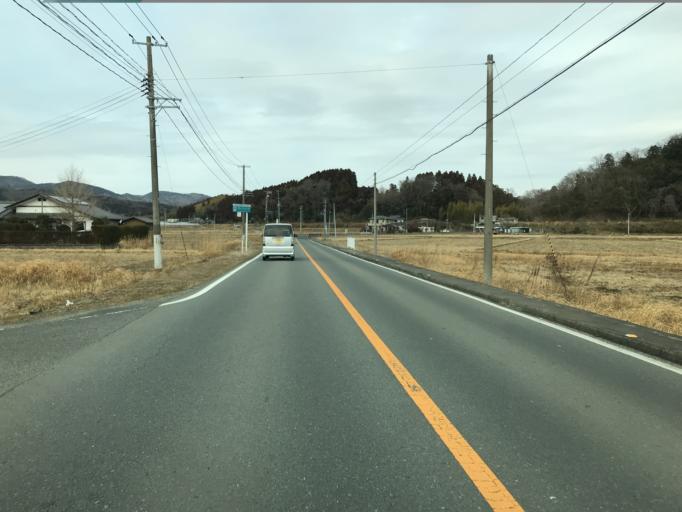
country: JP
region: Fukushima
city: Iwaki
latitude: 37.0899
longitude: 140.8742
